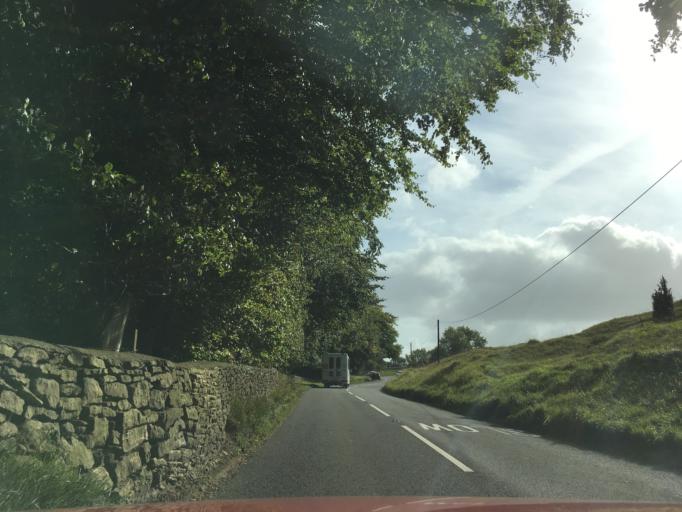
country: GB
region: England
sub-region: Gloucestershire
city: Nailsworth
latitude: 51.7258
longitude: -2.2442
